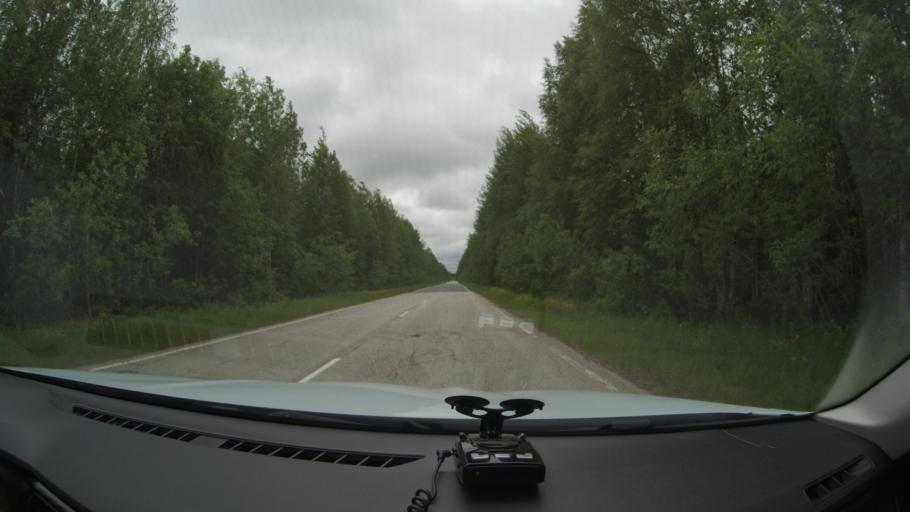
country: RU
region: Komi Republic
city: Nizhniy Odes
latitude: 63.6234
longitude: 54.6174
